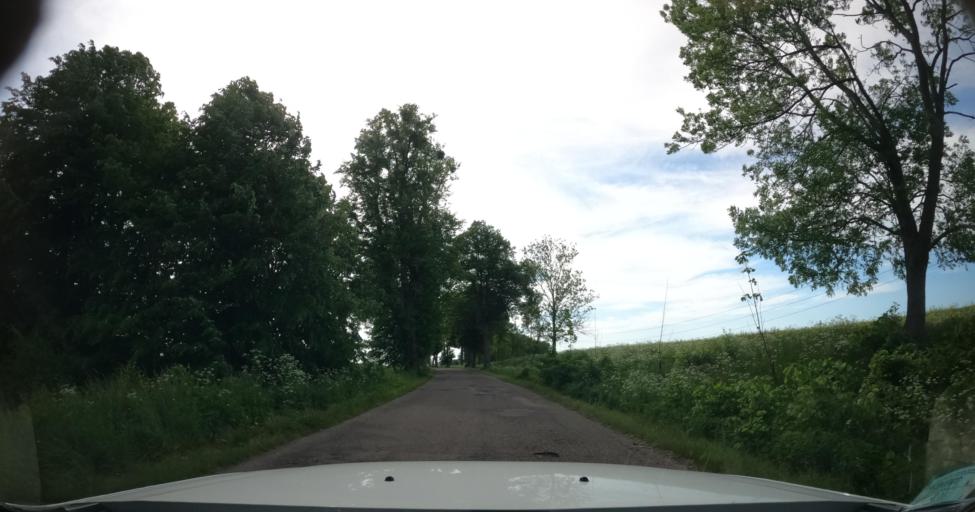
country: PL
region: Warmian-Masurian Voivodeship
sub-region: Powiat ostrodzki
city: Milakowo
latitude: 54.0184
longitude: 20.0406
